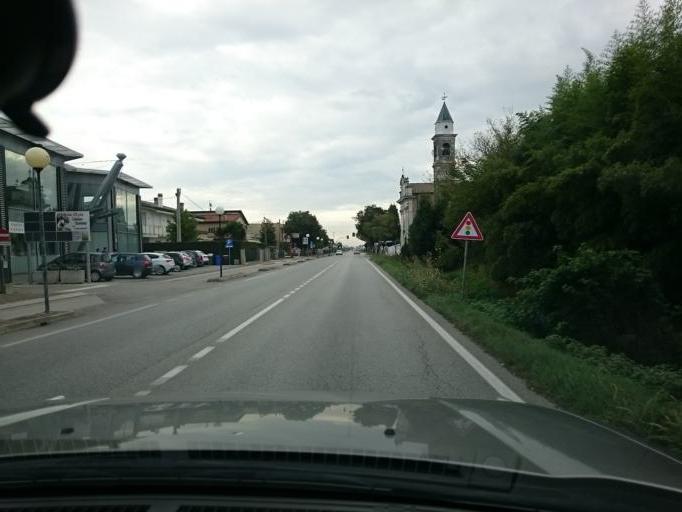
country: IT
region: Veneto
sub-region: Provincia di Padova
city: Sant'Angelo di Piove di Sacco
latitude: 45.3226
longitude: 11.9975
